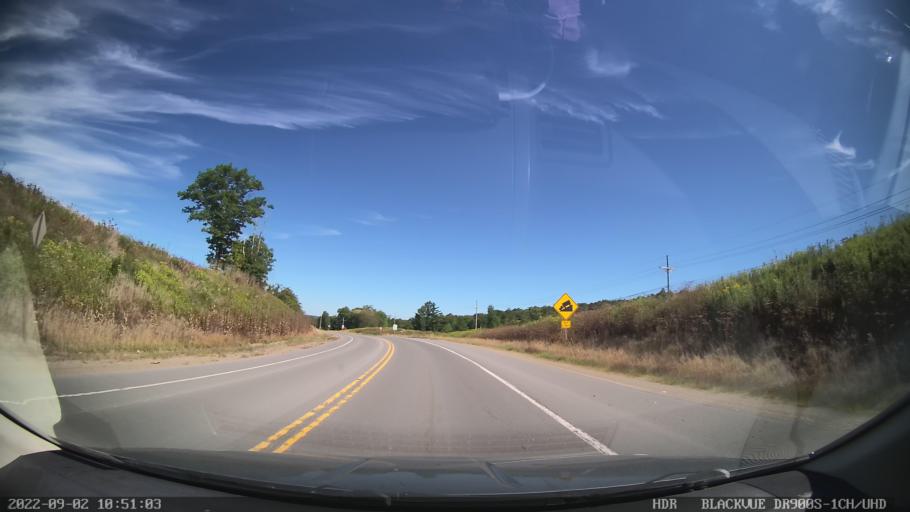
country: US
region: Pennsylvania
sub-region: Tioga County
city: Blossburg
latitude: 41.6216
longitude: -77.1174
